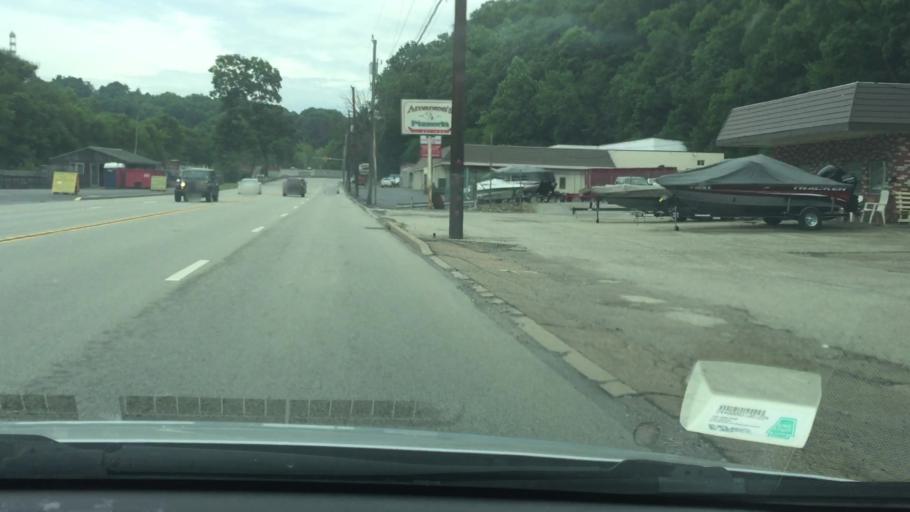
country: US
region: Pennsylvania
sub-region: Allegheny County
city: Glenshaw
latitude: 40.5342
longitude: -79.9601
